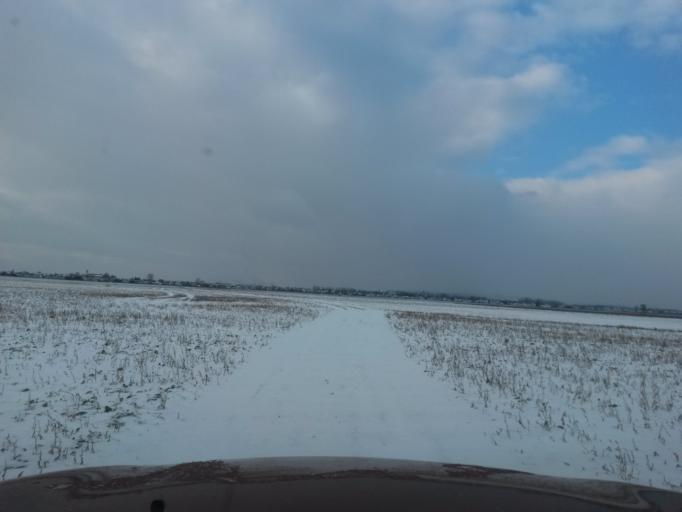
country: SK
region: Kosicky
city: Kosice
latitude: 48.6348
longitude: 21.3287
